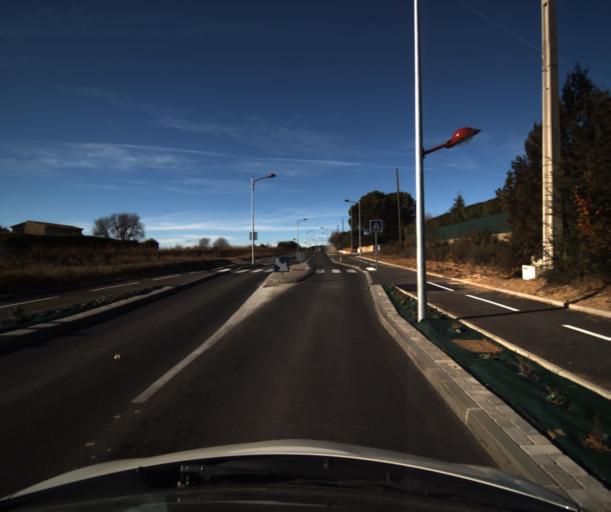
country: FR
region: Provence-Alpes-Cote d'Azur
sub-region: Departement du Vaucluse
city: Pertuis
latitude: 43.6973
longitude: 5.4804
